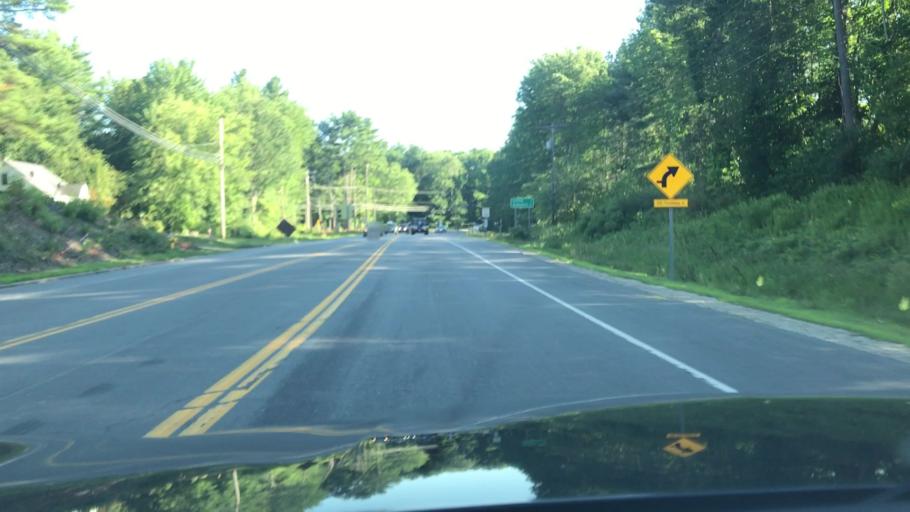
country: US
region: New Hampshire
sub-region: Strafford County
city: Durham
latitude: 43.1378
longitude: -70.9115
